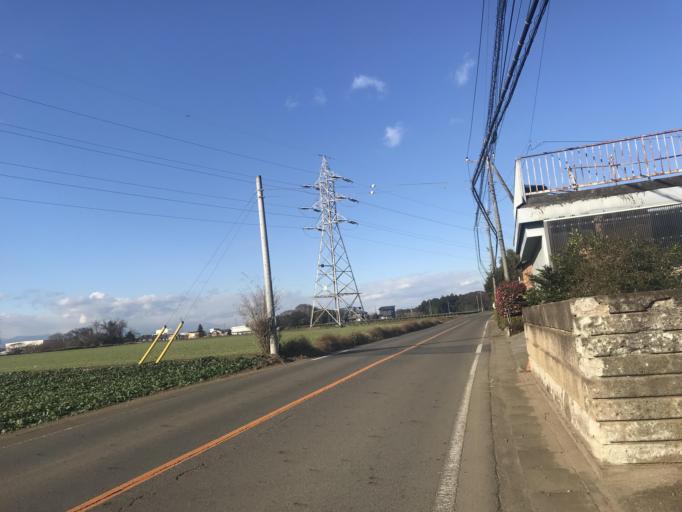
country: JP
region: Tochigi
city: Kaminokawa
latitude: 36.4094
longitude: 139.8771
